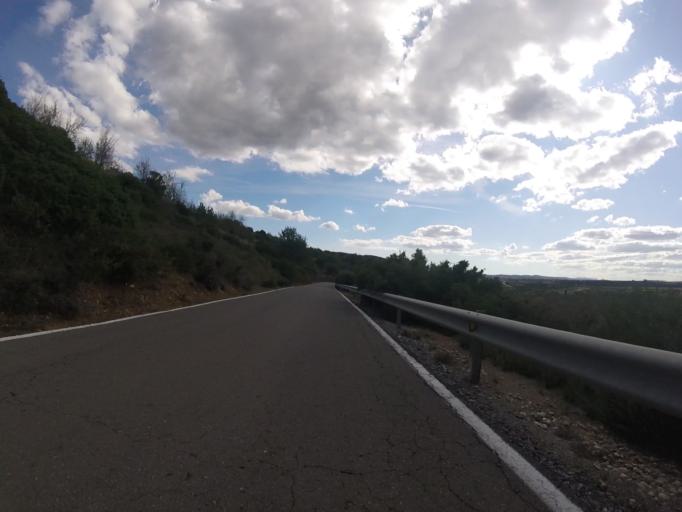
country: ES
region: Valencia
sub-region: Provincia de Castello
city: Cuevas de Vinroma
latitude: 40.3559
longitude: 0.1264
